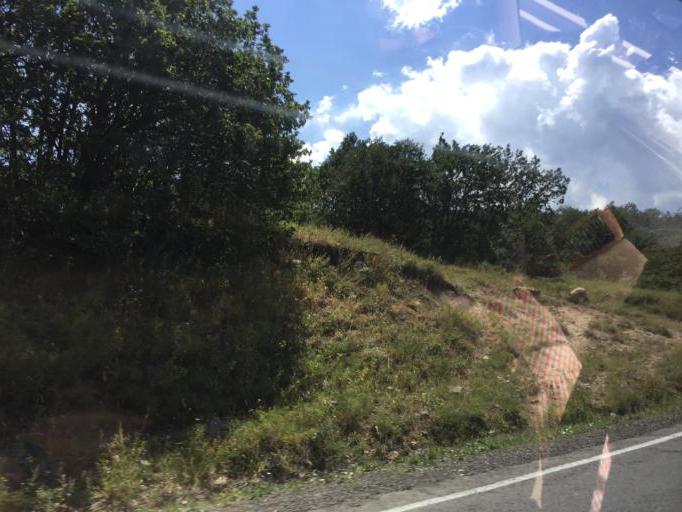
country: AM
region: Vayots' Dzori Marz
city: Jermuk
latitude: 39.7101
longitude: 45.6758
